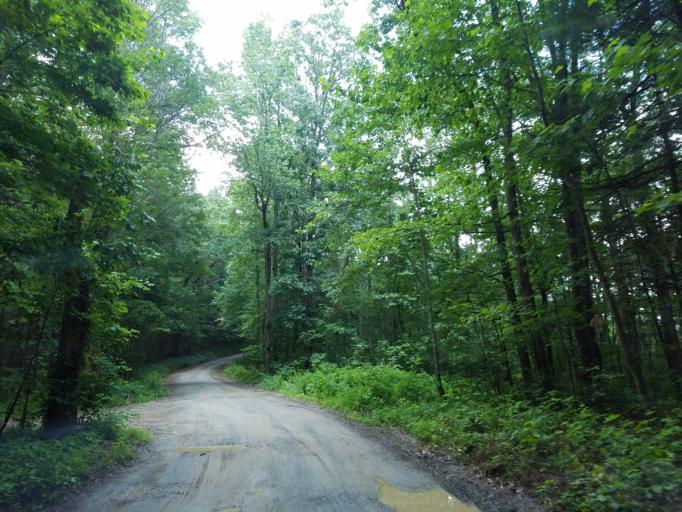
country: US
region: Georgia
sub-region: Fannin County
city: Blue Ridge
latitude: 34.6490
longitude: -84.2154
